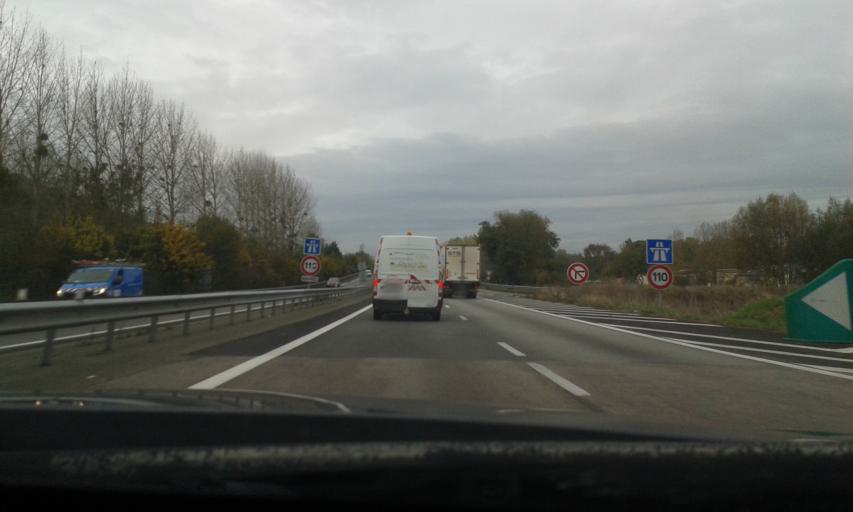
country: FR
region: Haute-Normandie
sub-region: Departement de l'Eure
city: Acquigny
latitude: 49.1803
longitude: 1.1701
